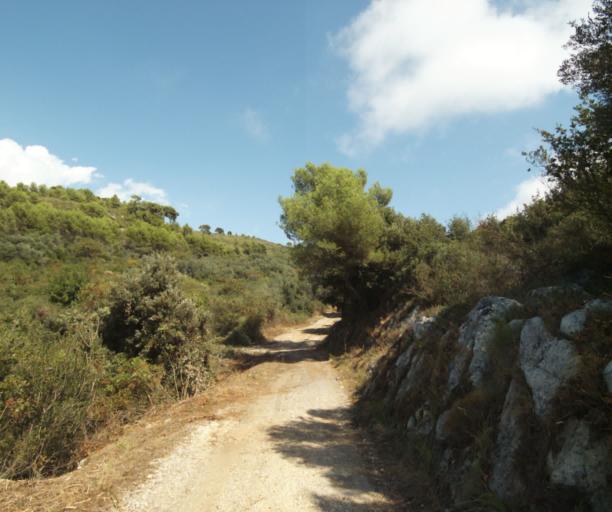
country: FR
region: Provence-Alpes-Cote d'Azur
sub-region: Departement des Alpes-Maritimes
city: Drap
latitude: 43.7541
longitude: 7.3488
